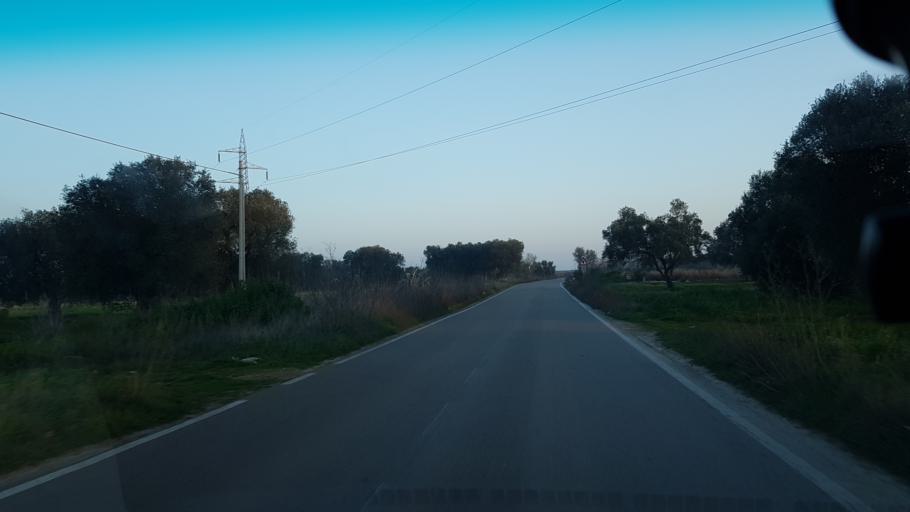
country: IT
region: Apulia
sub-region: Provincia di Brindisi
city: San Vito dei Normanni
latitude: 40.6389
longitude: 17.7799
